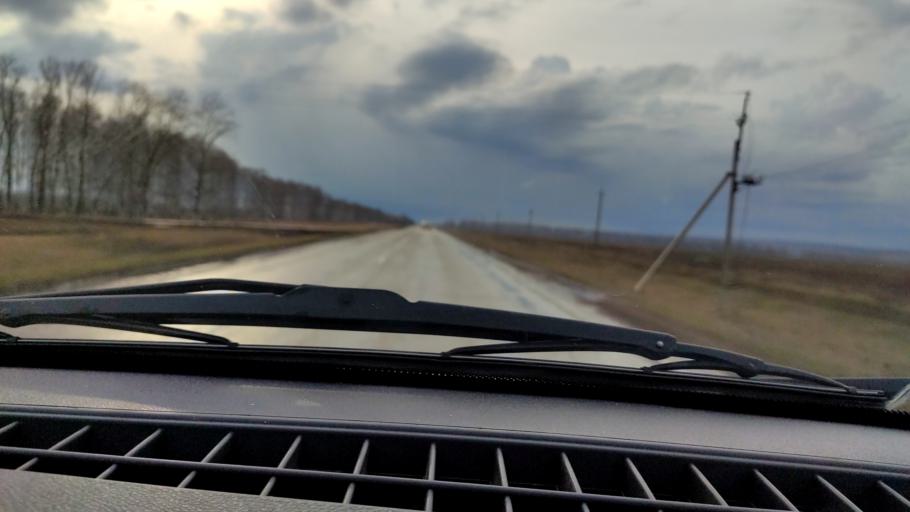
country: RU
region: Bashkortostan
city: Kushnarenkovo
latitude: 55.1048
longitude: 55.0171
